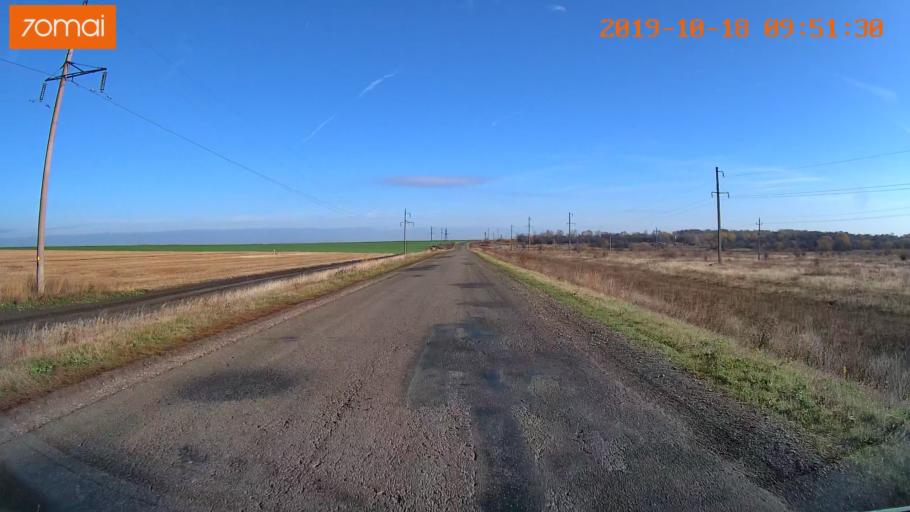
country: RU
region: Tula
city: Kazachka
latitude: 53.3415
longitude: 38.2937
